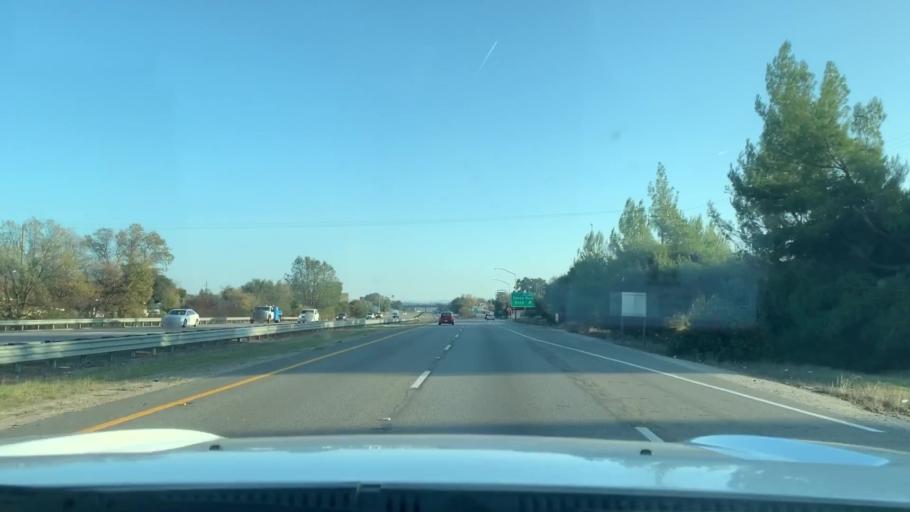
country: US
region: California
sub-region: San Luis Obispo County
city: Atascadero
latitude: 35.4717
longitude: -120.6559
